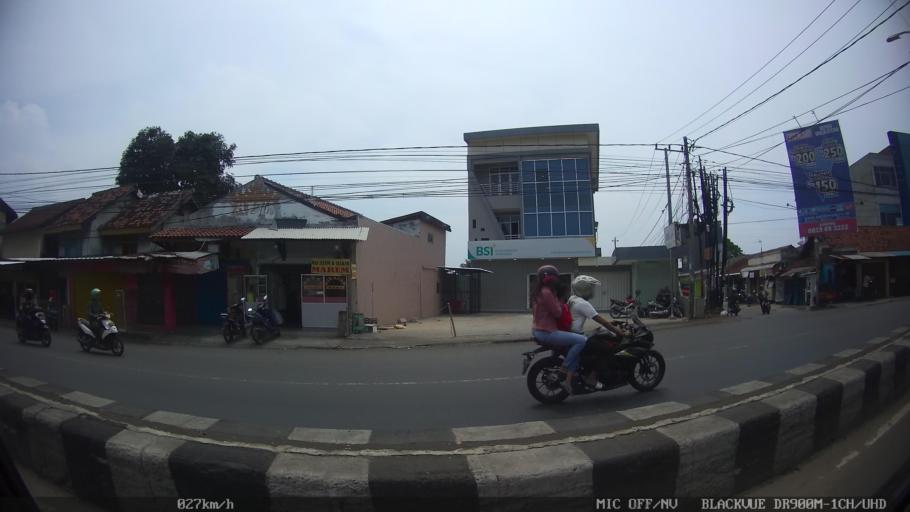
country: ID
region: Lampung
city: Bandarlampung
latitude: -5.4081
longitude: 105.2693
